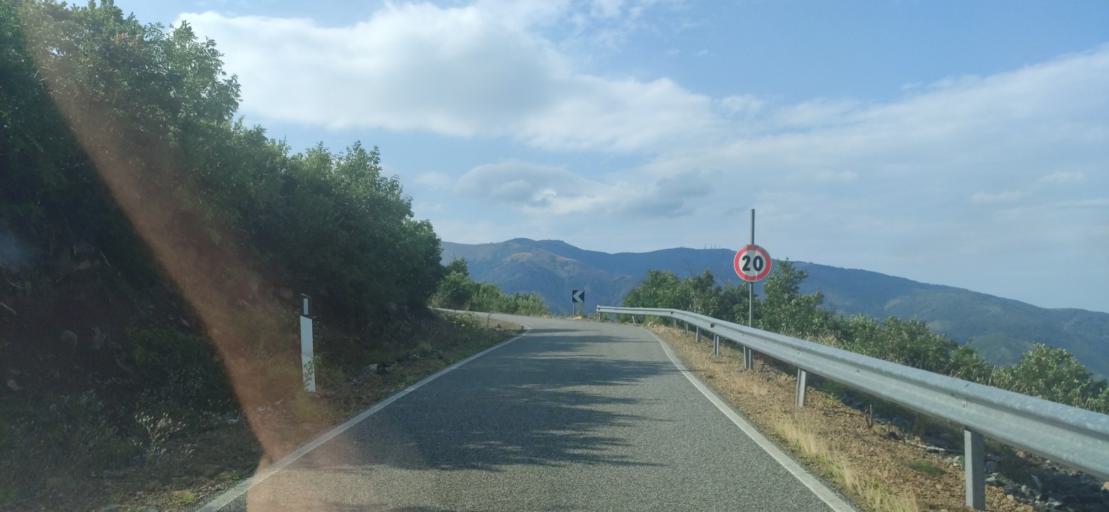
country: AL
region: Shkoder
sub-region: Rrethi i Pukes
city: Iballe
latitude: 42.1689
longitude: 20.0029
